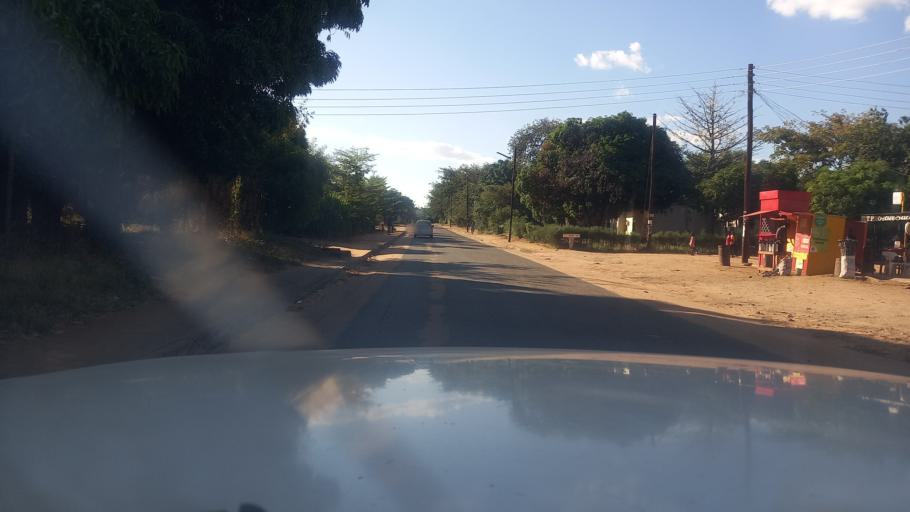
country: ZM
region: Southern
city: Livingstone
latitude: -17.8381
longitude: 25.8663
